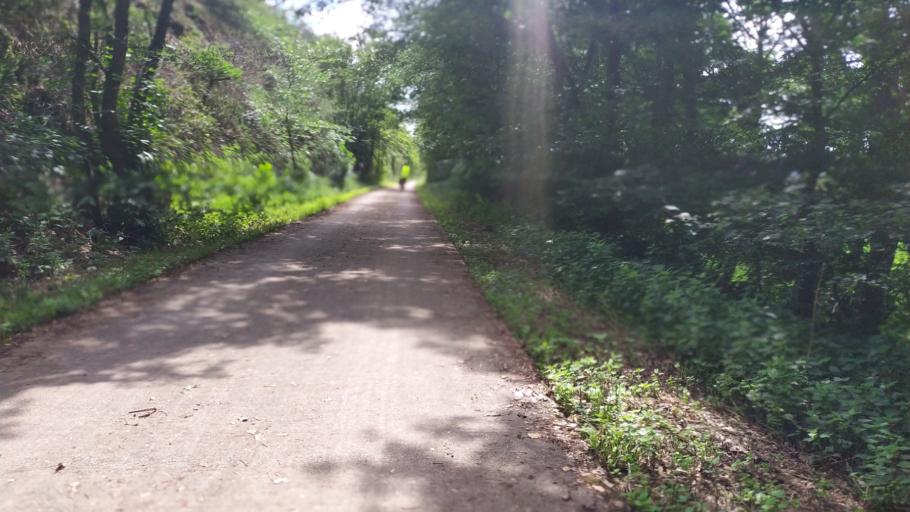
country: BE
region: Wallonia
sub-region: Province du Luxembourg
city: Wellin
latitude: 50.1549
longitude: 5.1259
